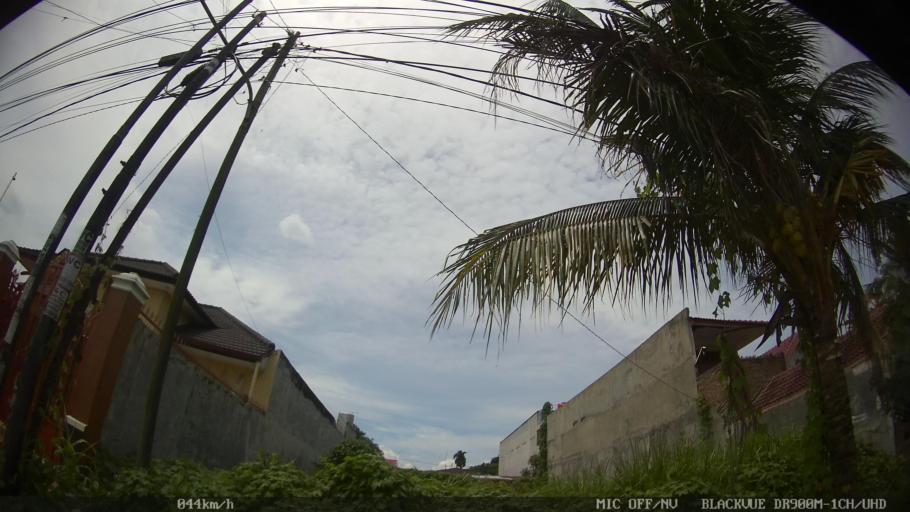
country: ID
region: North Sumatra
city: Medan
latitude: 3.5550
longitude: 98.6552
